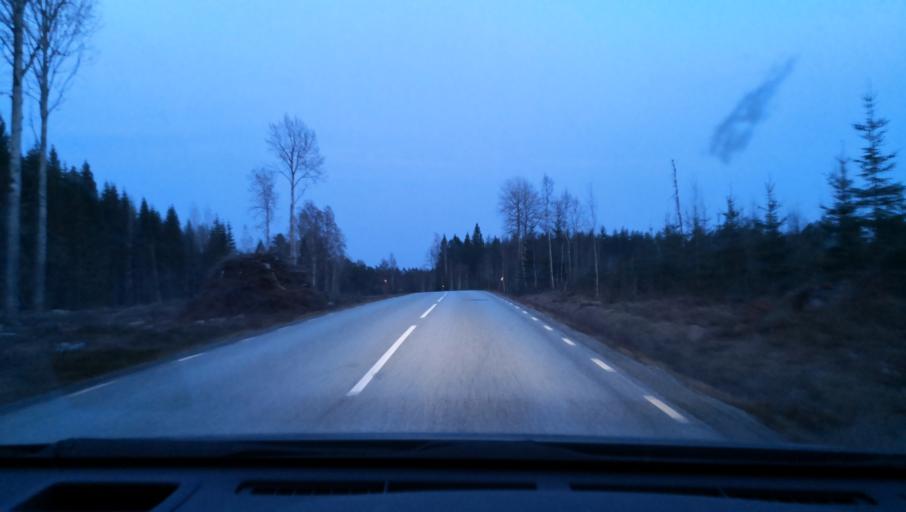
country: SE
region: OErebro
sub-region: Lindesbergs Kommun
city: Frovi
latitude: 59.5906
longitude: 15.4301
